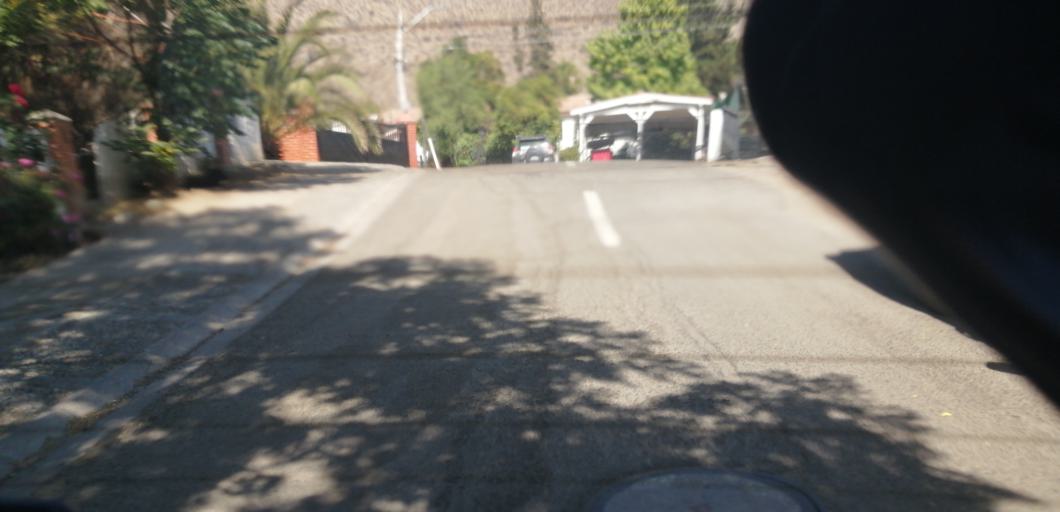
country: CL
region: Santiago Metropolitan
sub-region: Provincia de Santiago
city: Lo Prado
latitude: -33.4577
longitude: -70.8192
